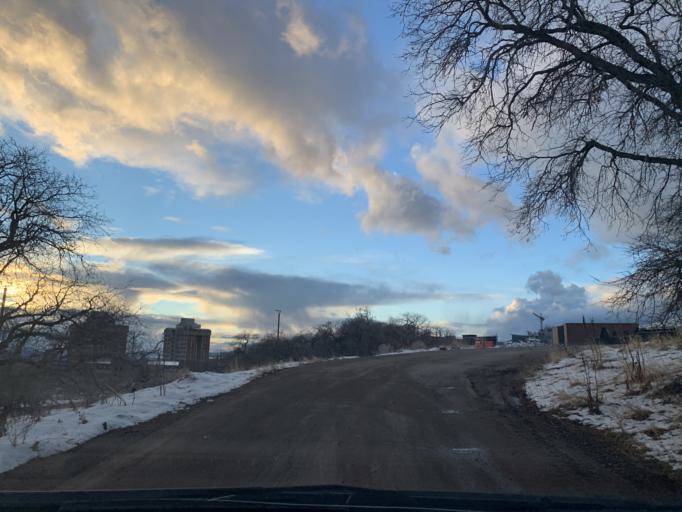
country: US
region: Utah
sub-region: Salt Lake County
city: Canyon Rim
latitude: 40.7677
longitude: -111.8274
